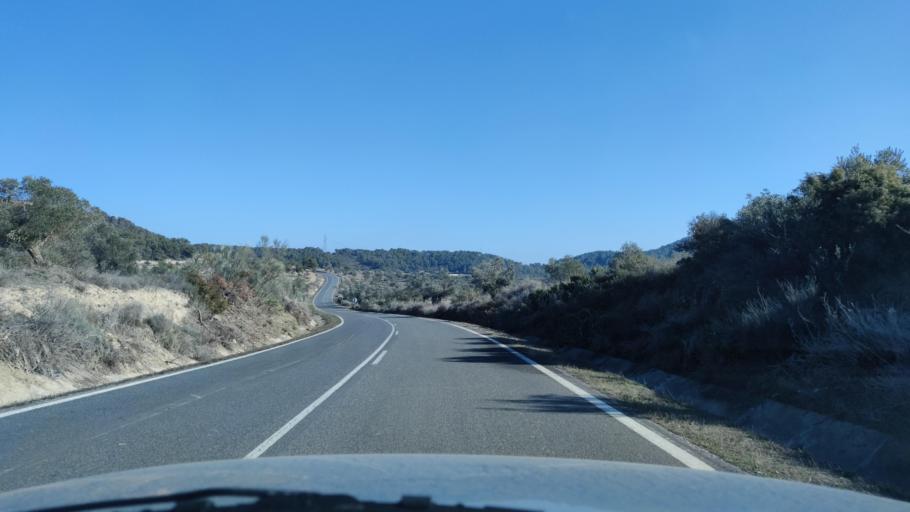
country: ES
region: Catalonia
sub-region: Provincia de Lleida
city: Maials
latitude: 41.3332
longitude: 0.4445
